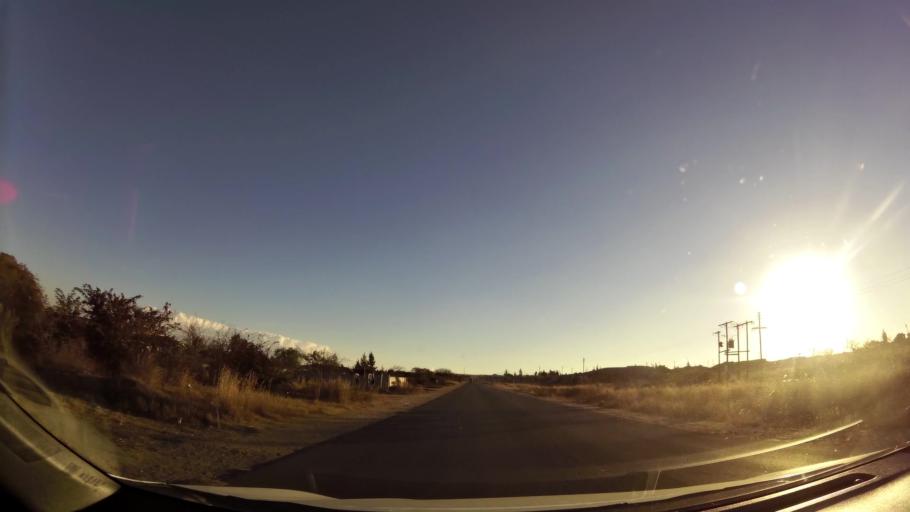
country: ZA
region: Limpopo
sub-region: Capricorn District Municipality
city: Polokwane
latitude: -23.8376
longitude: 29.3552
